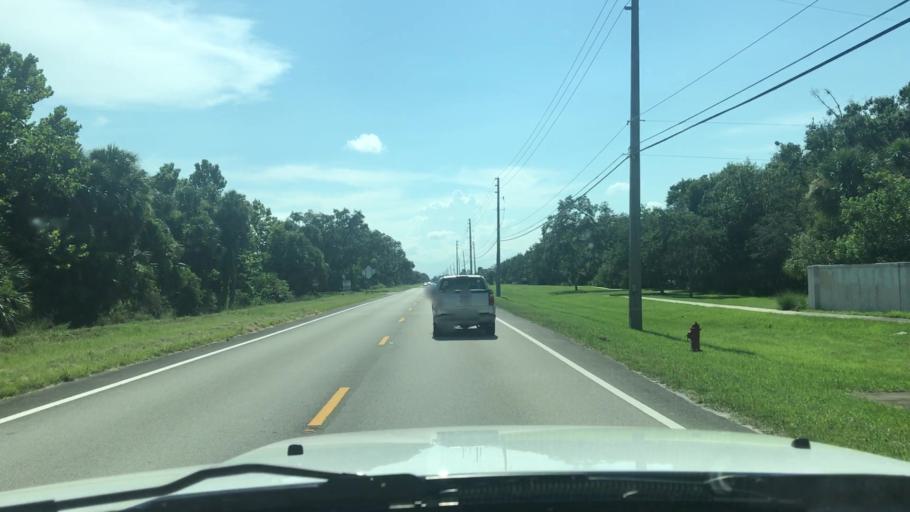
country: US
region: Florida
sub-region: Indian River County
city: West Vero Corridor
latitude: 27.6462
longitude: -80.4503
